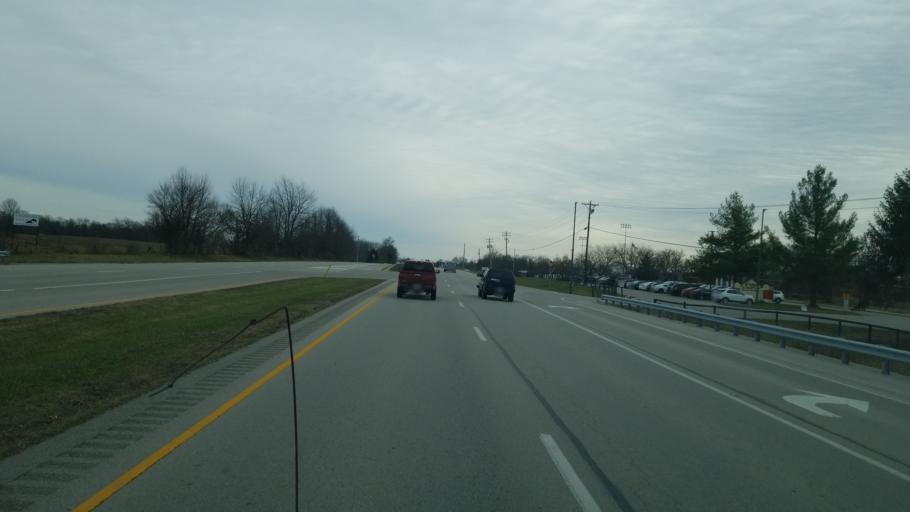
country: US
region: Kentucky
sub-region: Bourbon County
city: Paris
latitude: 38.2252
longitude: -84.2438
